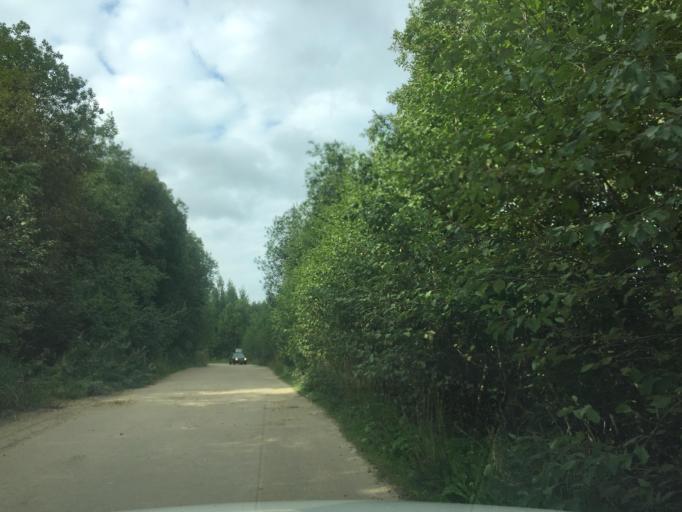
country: RU
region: Leningrad
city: Siverskiy
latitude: 59.2987
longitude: 30.0265
